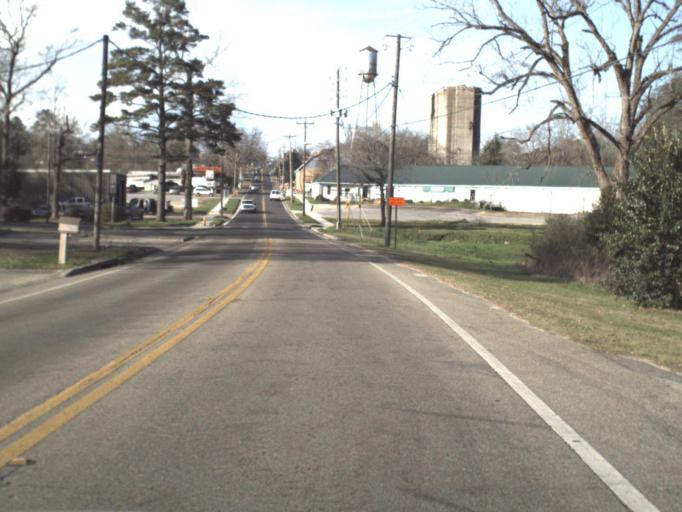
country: US
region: Florida
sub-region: Jackson County
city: Marianna
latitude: 30.7682
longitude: -85.2268
